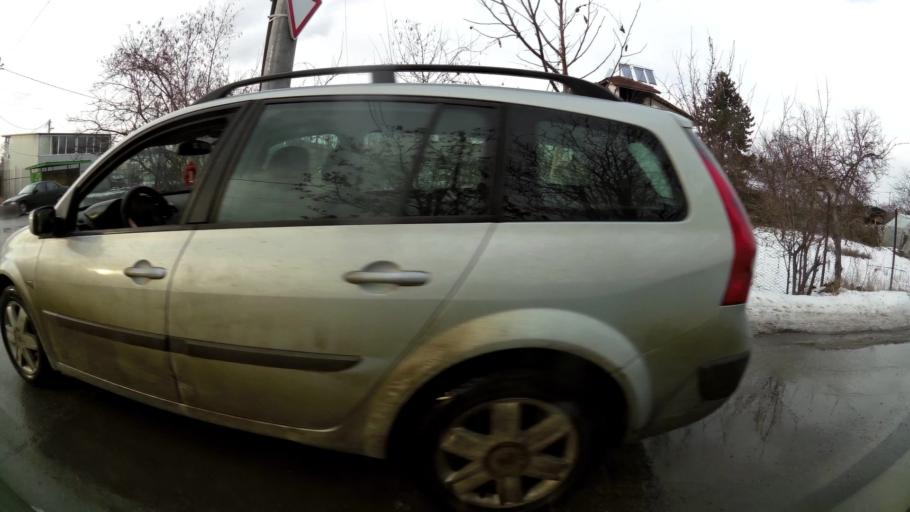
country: BG
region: Sofia-Capital
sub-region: Stolichna Obshtina
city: Sofia
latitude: 42.7287
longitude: 23.3445
